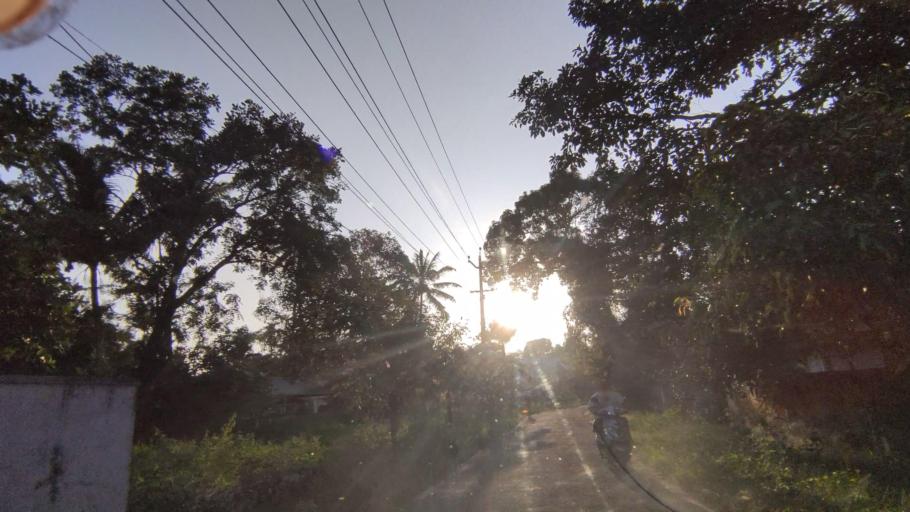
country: IN
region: Kerala
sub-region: Alappuzha
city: Shertallai
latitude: 9.6470
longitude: 76.3395
